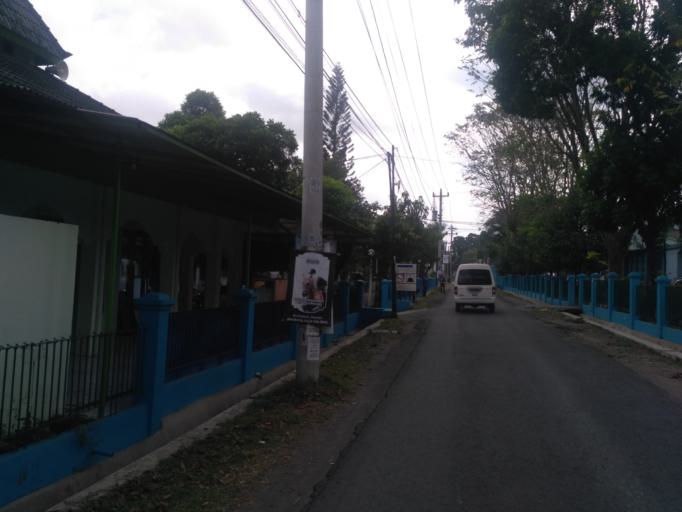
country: ID
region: Daerah Istimewa Yogyakarta
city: Melati
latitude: -7.7516
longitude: 110.3605
